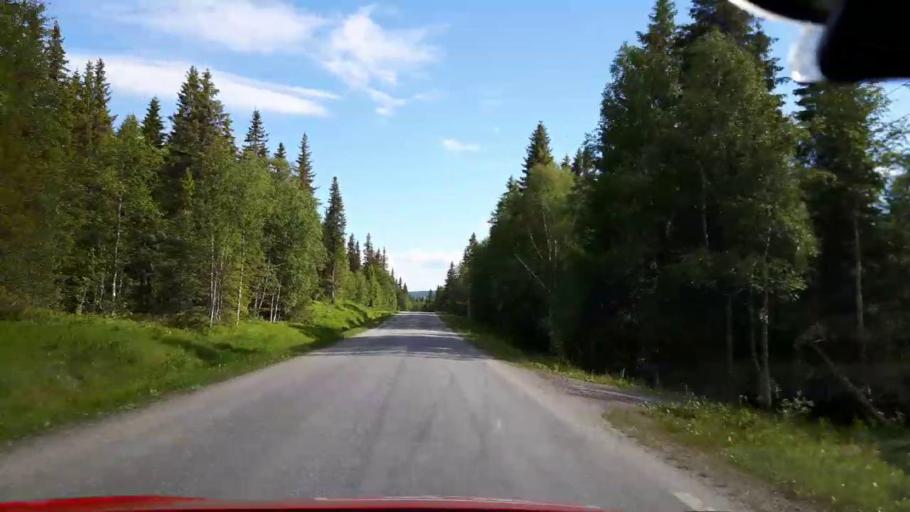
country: SE
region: Jaemtland
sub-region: Krokoms Kommun
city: Valla
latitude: 63.7758
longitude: 14.0449
